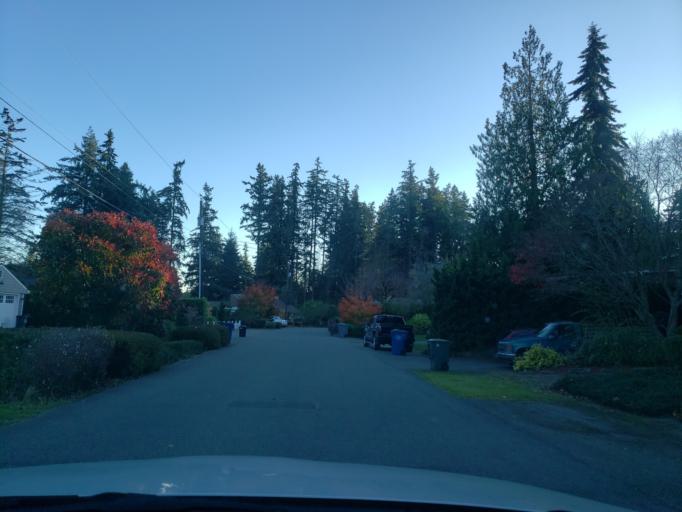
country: US
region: Washington
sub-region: Snohomish County
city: Woodway
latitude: 47.7828
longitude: -122.3809
